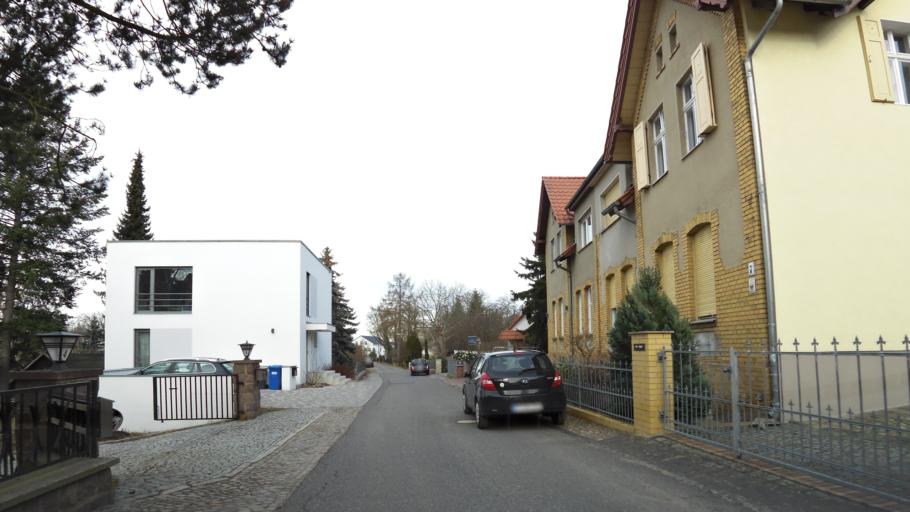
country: DE
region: Brandenburg
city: Michendorf
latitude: 52.3496
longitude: 13.0124
